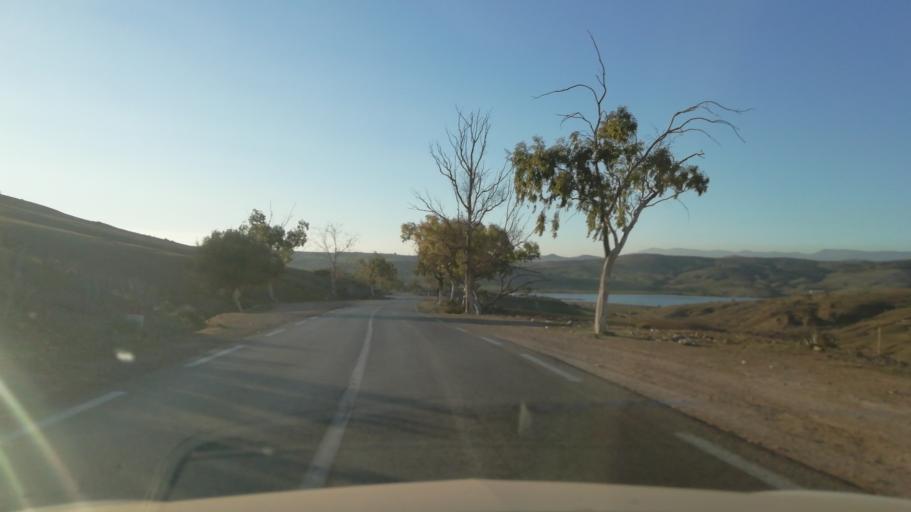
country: DZ
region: Tlemcen
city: Nedroma
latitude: 34.8282
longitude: -1.6410
